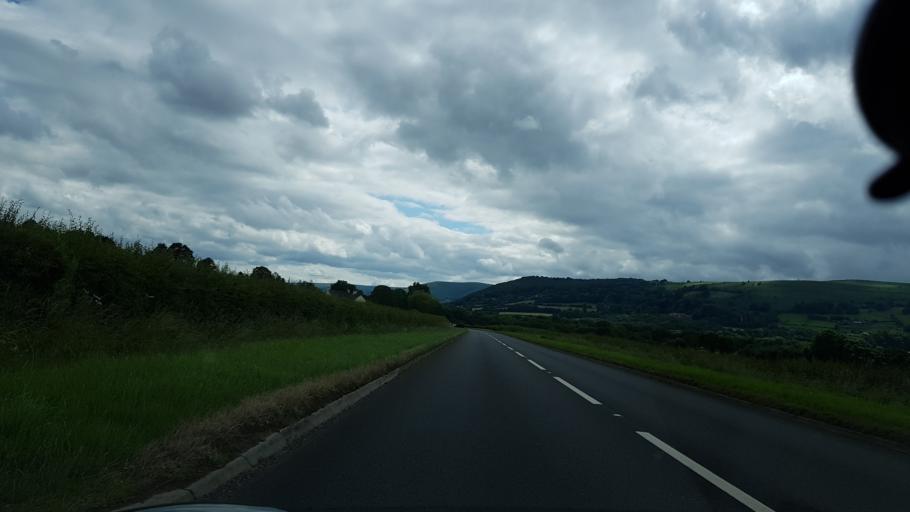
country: GB
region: Wales
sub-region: Monmouthshire
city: Abergavenny
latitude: 51.8630
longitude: -2.9947
